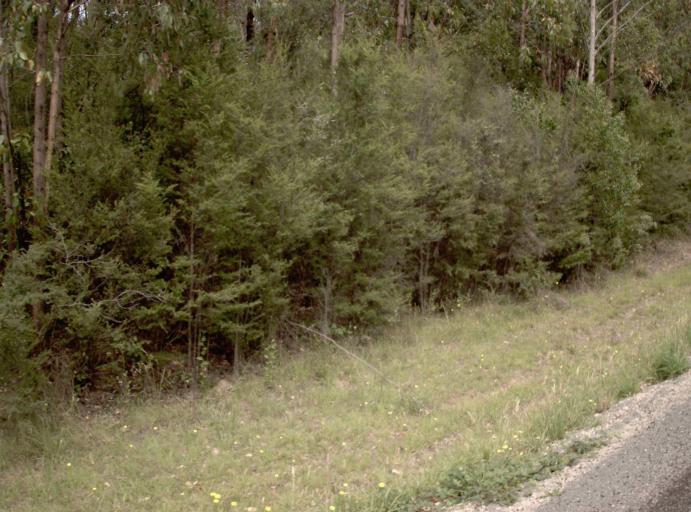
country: AU
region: Victoria
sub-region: Latrobe
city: Traralgon
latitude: -38.1062
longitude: 146.4506
